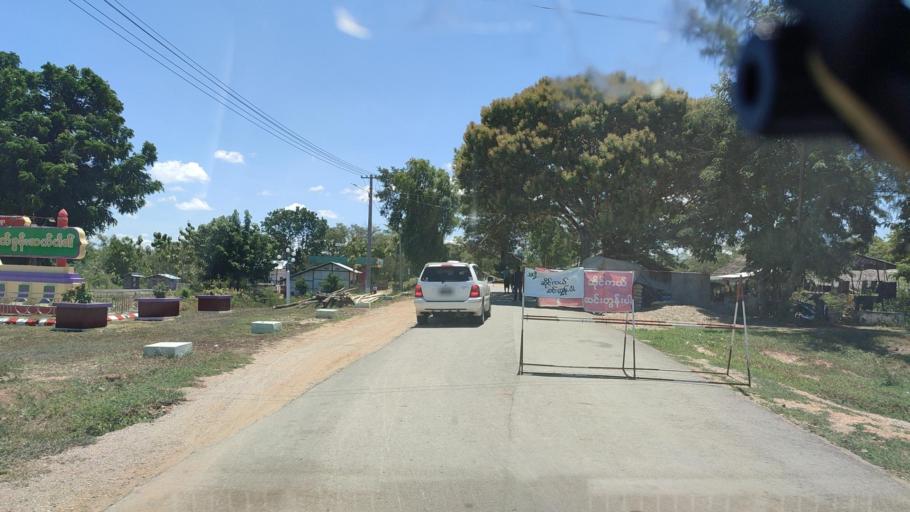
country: MM
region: Magway
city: Myaydo
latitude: 19.7297
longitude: 95.1727
